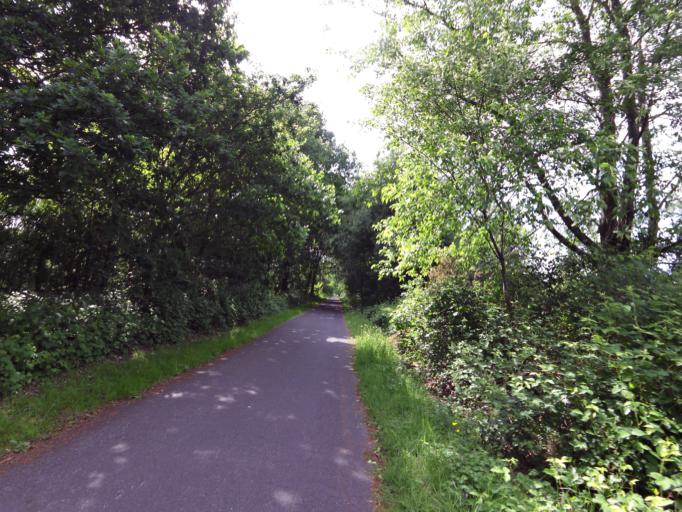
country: BE
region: Flanders
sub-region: Provincie West-Vlaanderen
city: Beernem
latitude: 51.1406
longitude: 3.3192
